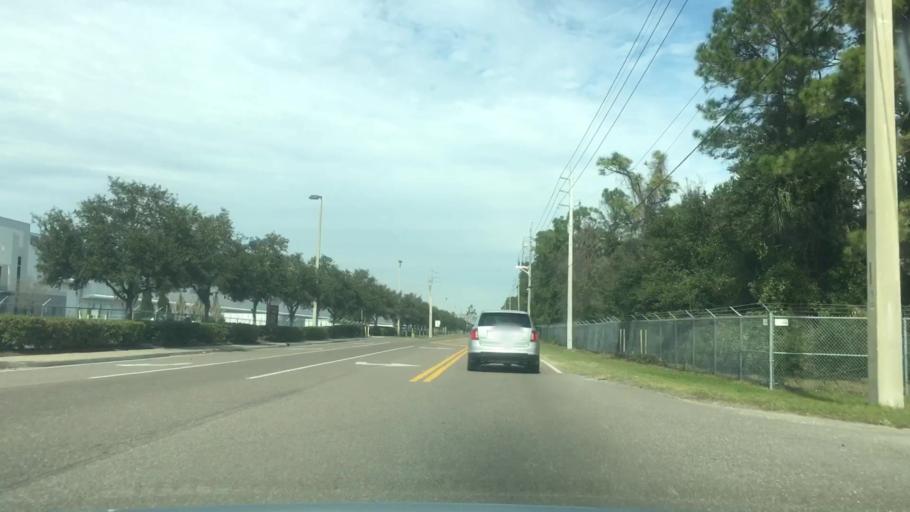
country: US
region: Florida
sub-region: Duval County
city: Jacksonville
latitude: 30.4413
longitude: -81.5581
